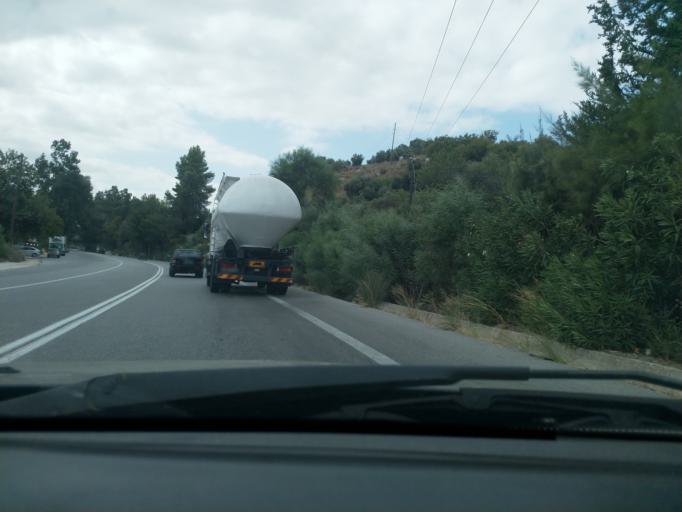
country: GR
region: Crete
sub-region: Nomos Chanias
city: Georgioupolis
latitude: 35.3783
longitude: 24.2056
